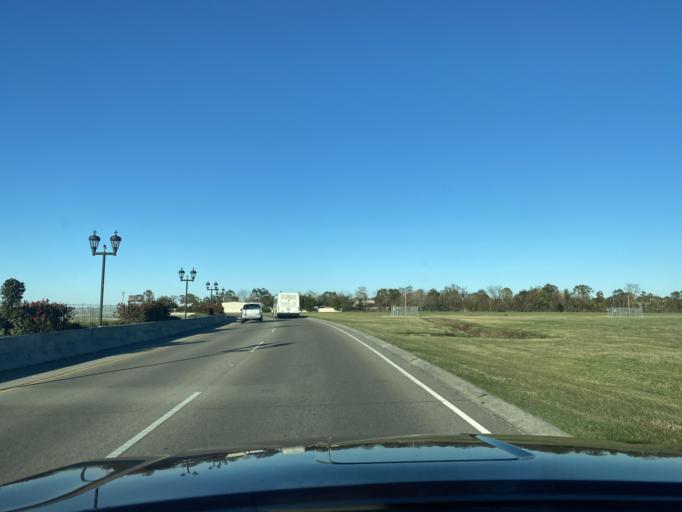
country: US
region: Louisiana
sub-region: Jefferson Parish
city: Kenner
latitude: 29.9874
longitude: -90.2485
